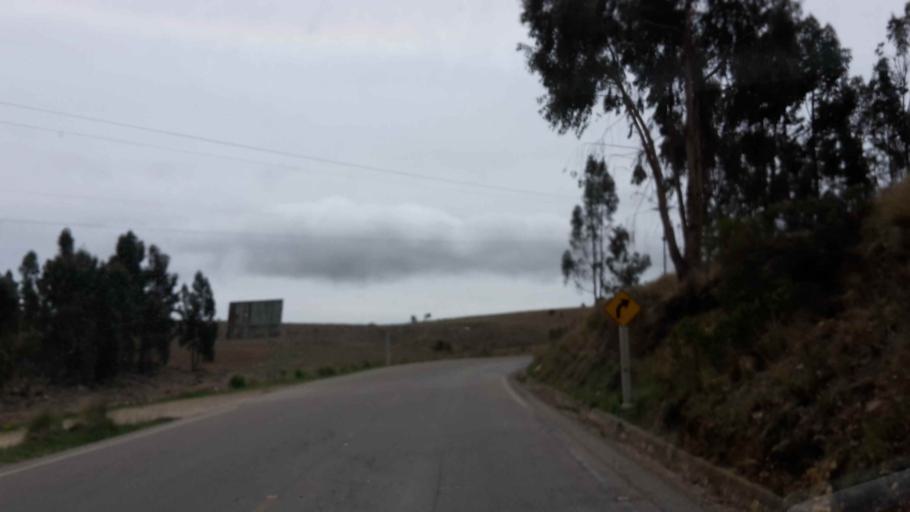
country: BO
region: Cochabamba
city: Arani
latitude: -17.4866
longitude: -65.6122
